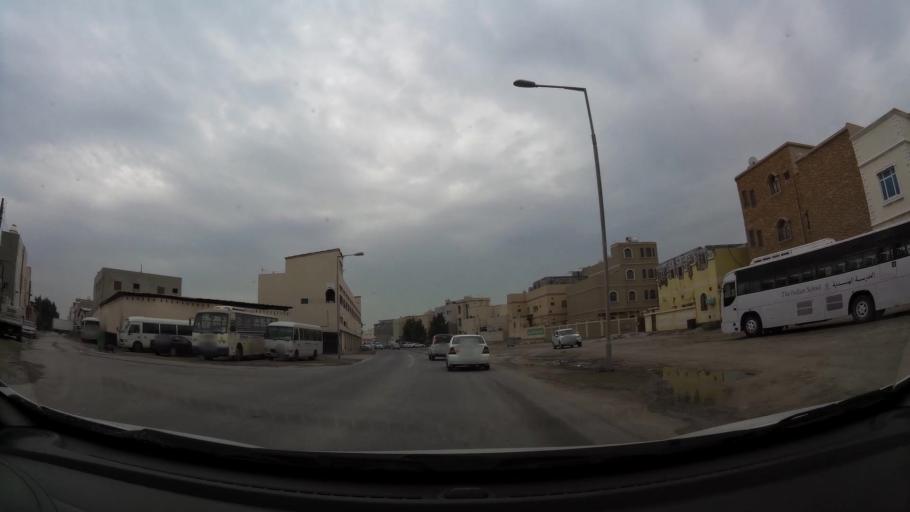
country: BH
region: Northern
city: Sitrah
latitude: 26.1685
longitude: 50.6153
